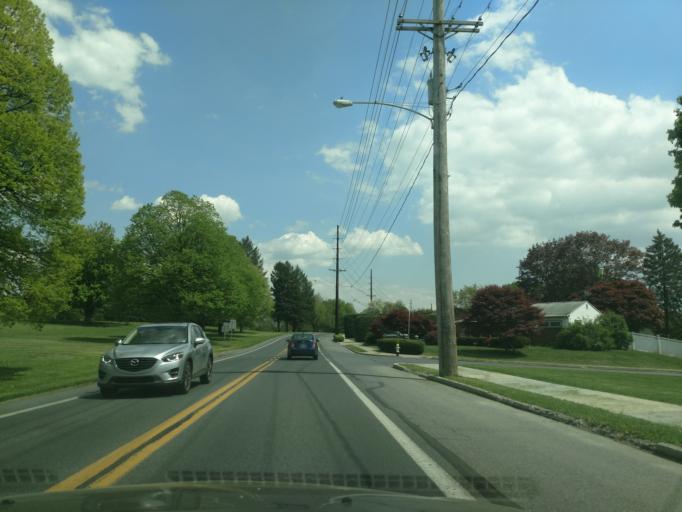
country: US
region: Pennsylvania
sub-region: Lebanon County
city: Hebron
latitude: 40.3370
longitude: -76.4022
